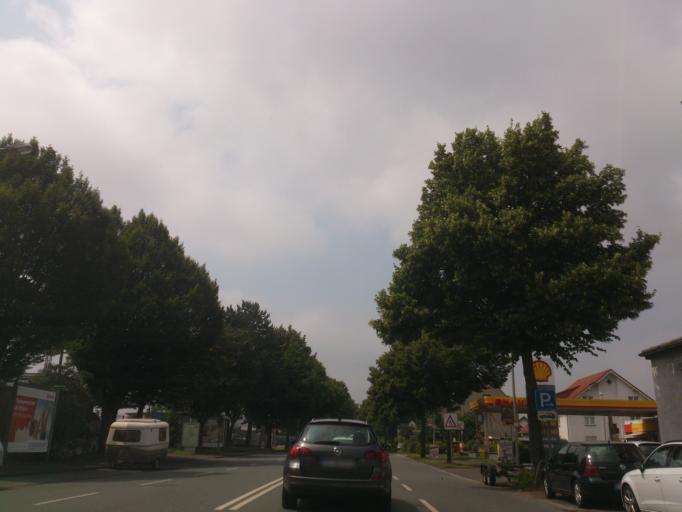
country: DE
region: North Rhine-Westphalia
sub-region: Regierungsbezirk Detmold
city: Paderborn
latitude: 51.7115
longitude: 8.7320
